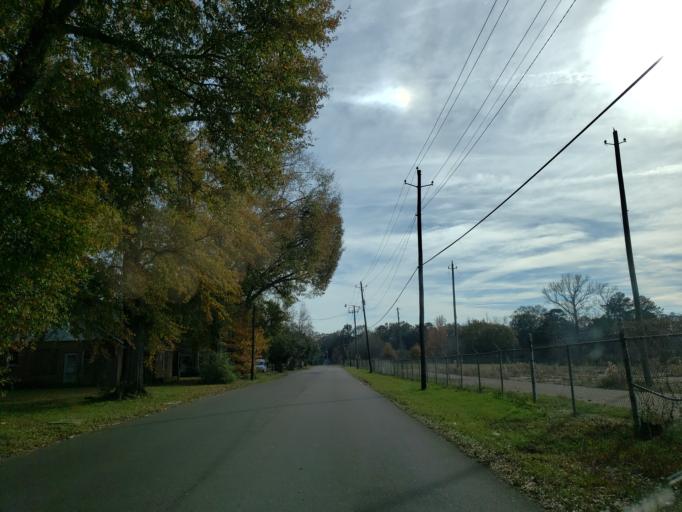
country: US
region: Mississippi
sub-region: Forrest County
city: Hattiesburg
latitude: 31.3375
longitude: -89.3043
